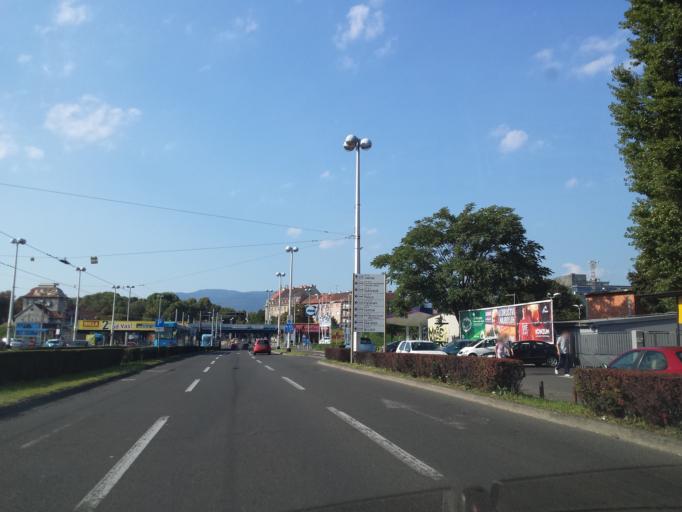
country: HR
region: Grad Zagreb
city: Zagreb - Centar
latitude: 45.8048
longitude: 15.9935
